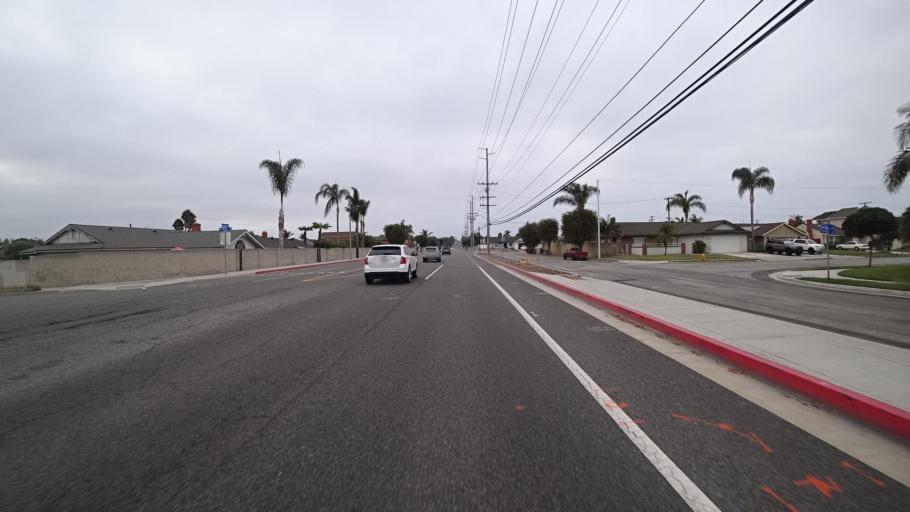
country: US
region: California
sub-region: Orange County
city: Huntington Beach
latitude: 33.7042
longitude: -118.0152
